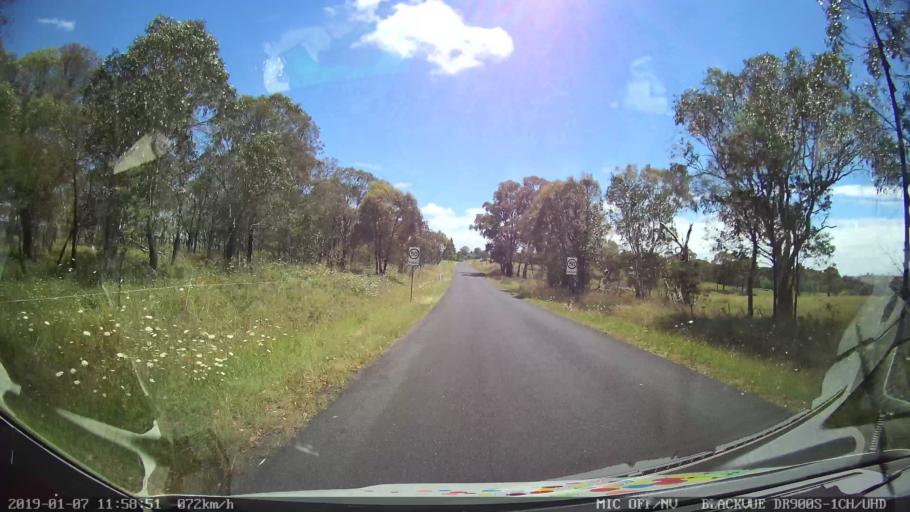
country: AU
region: New South Wales
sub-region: Guyra
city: Guyra
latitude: -30.2487
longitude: 151.6686
